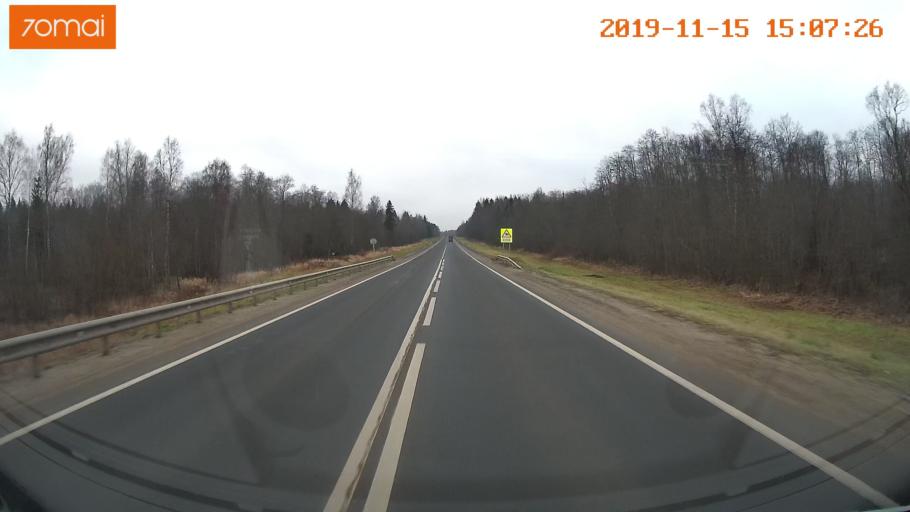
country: RU
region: Jaroslavl
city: Prechistoye
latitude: 58.3837
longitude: 40.2954
